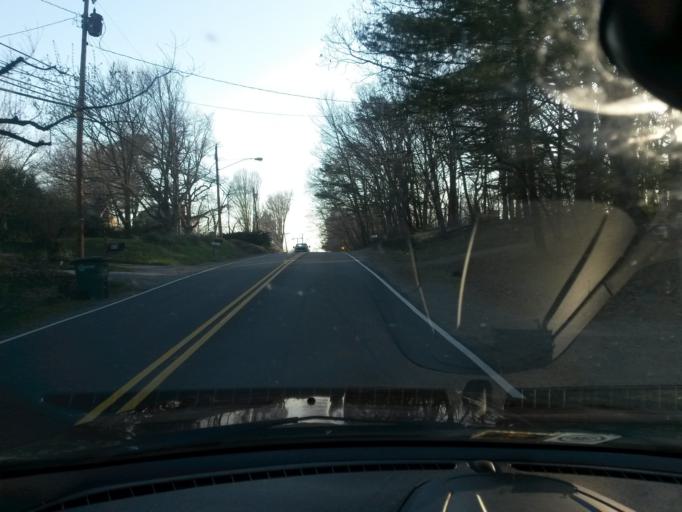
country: US
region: Virginia
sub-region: Montgomery County
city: Christiansburg
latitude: 37.1214
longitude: -80.4184
